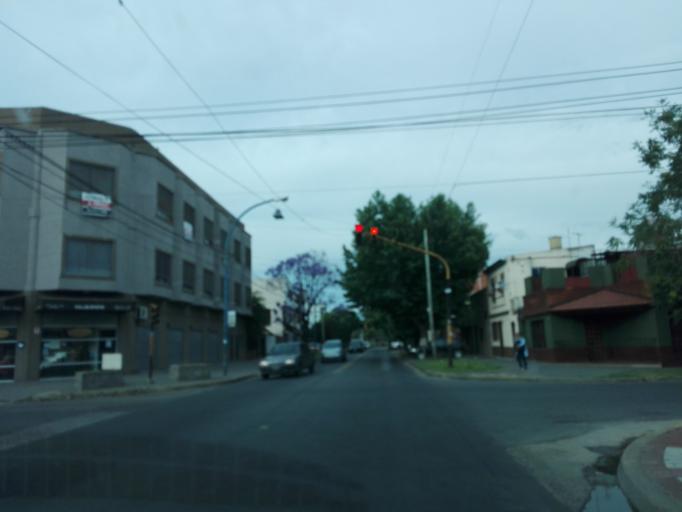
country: AR
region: Buenos Aires
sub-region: Partido de Lanus
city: Lanus
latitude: -34.7076
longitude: -58.3724
